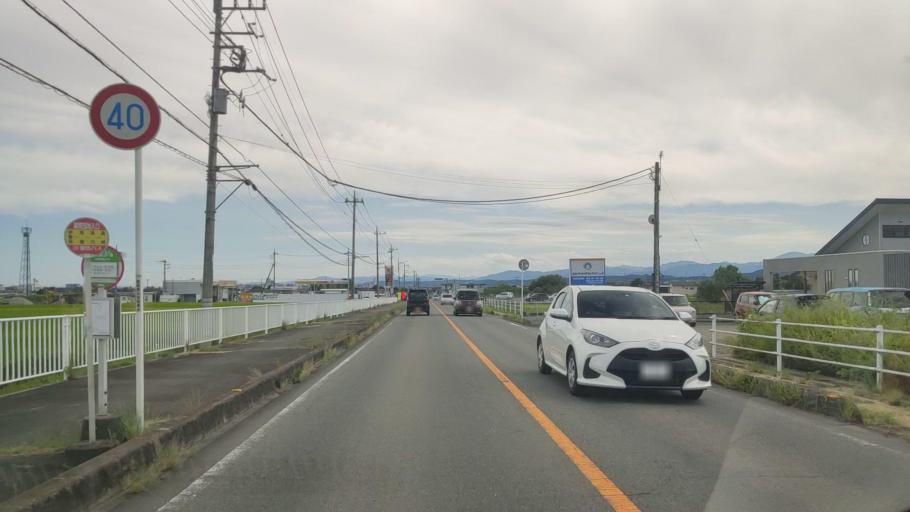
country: JP
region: Gunma
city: Kanekomachi
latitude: 36.3729
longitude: 138.9725
